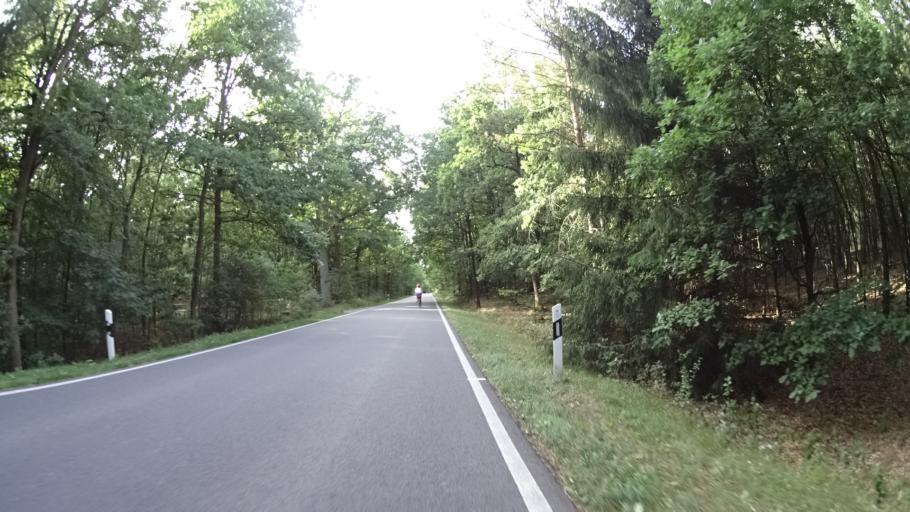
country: DE
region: Lower Saxony
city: Handeloh
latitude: 53.1733
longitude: 9.8897
